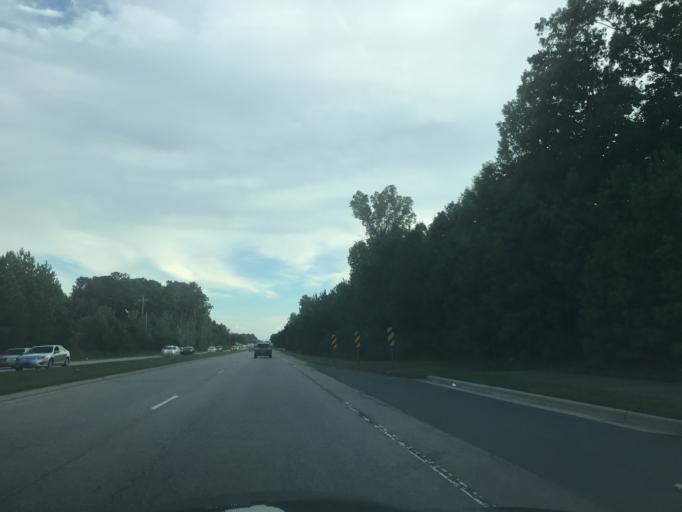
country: US
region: North Carolina
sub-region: Wake County
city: Green Level
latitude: 35.8105
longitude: -78.8724
